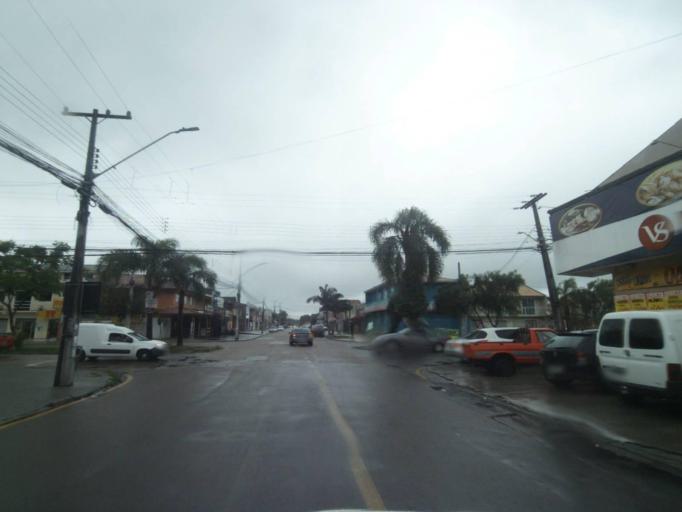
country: BR
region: Parana
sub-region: Araucaria
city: Araucaria
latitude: -25.5467
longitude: -49.3411
